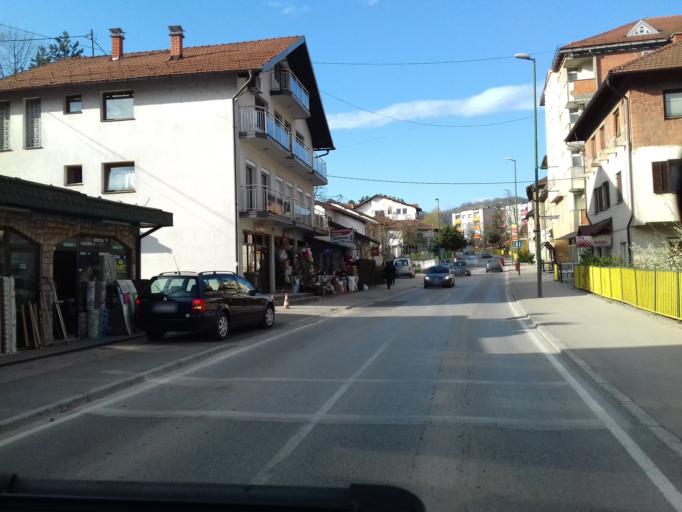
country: BA
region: Federation of Bosnia and Herzegovina
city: Tesanj
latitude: 44.6083
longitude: 17.9880
